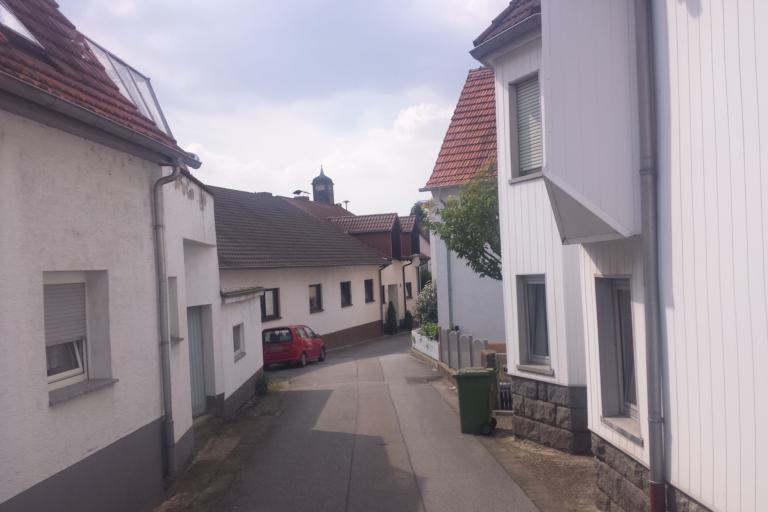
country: DE
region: Baden-Wuerttemberg
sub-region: Karlsruhe Region
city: Hemsbach
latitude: 49.5784
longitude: 8.6619
